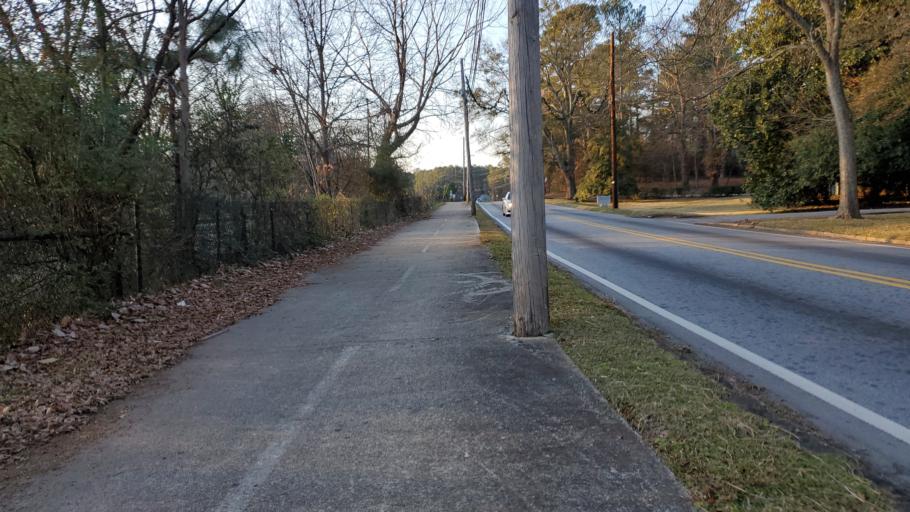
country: US
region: Georgia
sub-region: DeKalb County
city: Stone Mountain
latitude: 33.8121
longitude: -84.1734
